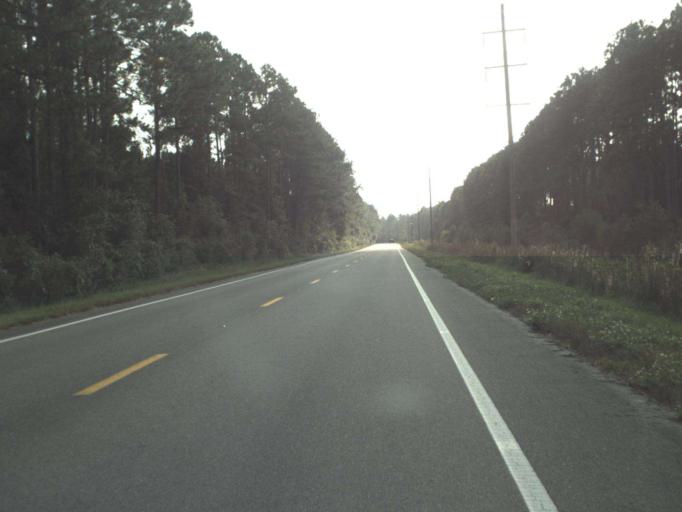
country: US
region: Florida
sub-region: Franklin County
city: Carrabelle
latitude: 29.9618
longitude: -84.5024
